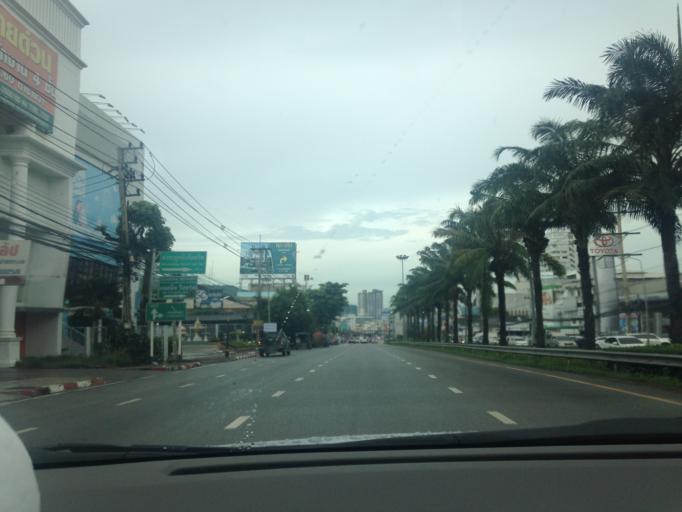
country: TH
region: Chon Buri
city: Si Racha
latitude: 13.1612
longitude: 100.9256
